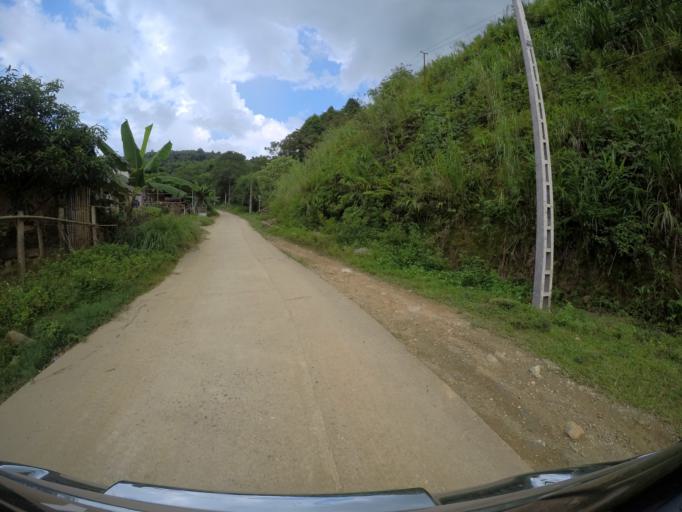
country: VN
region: Yen Bai
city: Son Thinh
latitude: 21.6549
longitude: 104.5072
